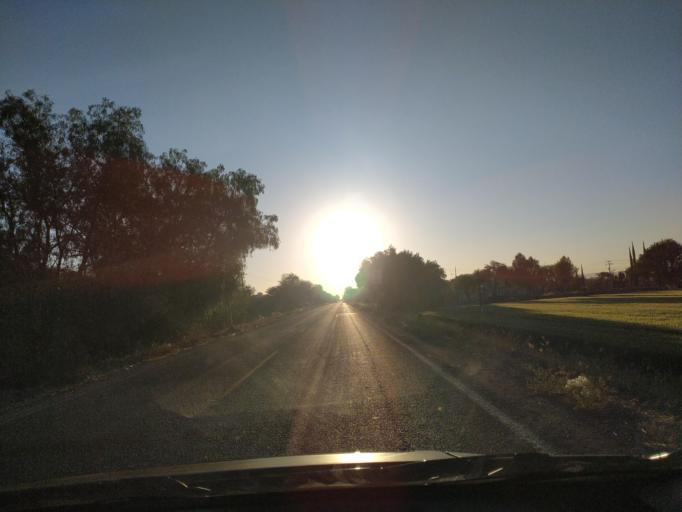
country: MX
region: Guanajuato
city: Ciudad Manuel Doblado
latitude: 20.7410
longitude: -101.9281
